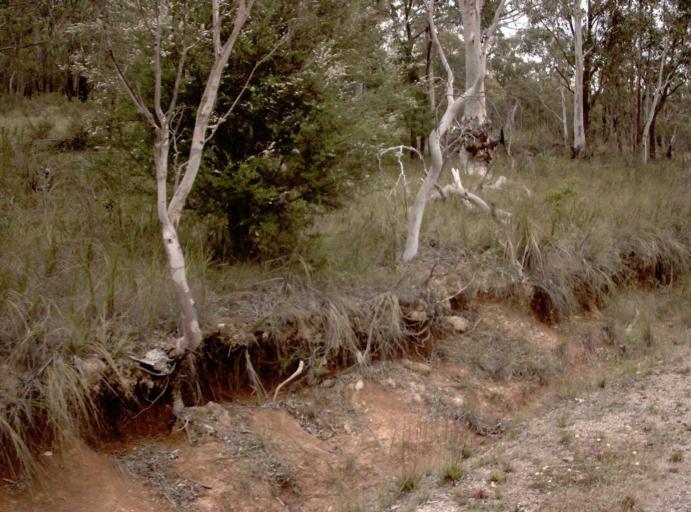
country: AU
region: Victoria
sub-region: East Gippsland
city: Bairnsdale
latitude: -37.6366
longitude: 147.2395
